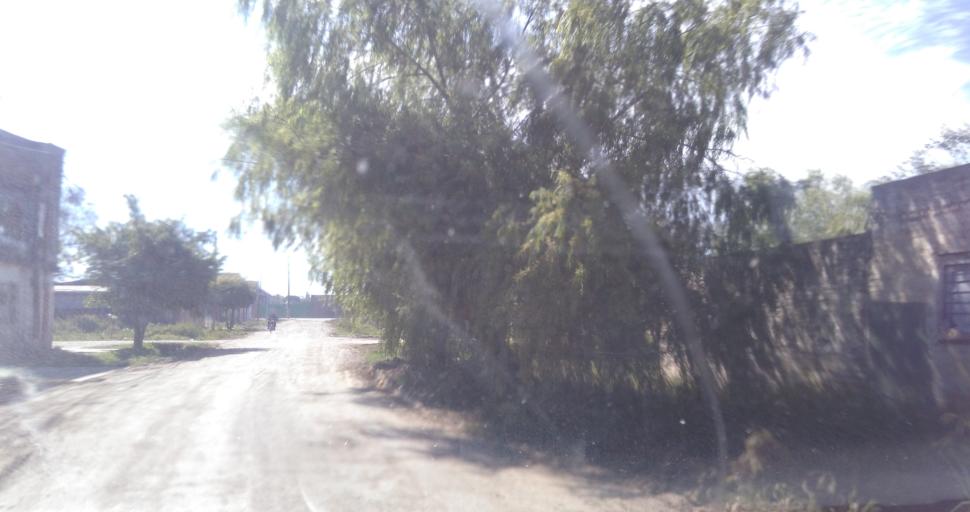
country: AR
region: Chaco
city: Fontana
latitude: -27.4342
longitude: -59.0225
